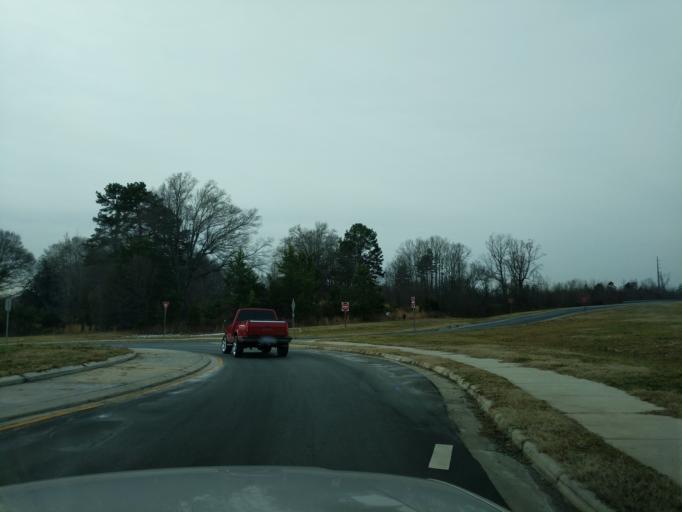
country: US
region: North Carolina
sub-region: Mecklenburg County
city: Huntersville
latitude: 35.3322
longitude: -80.9120
